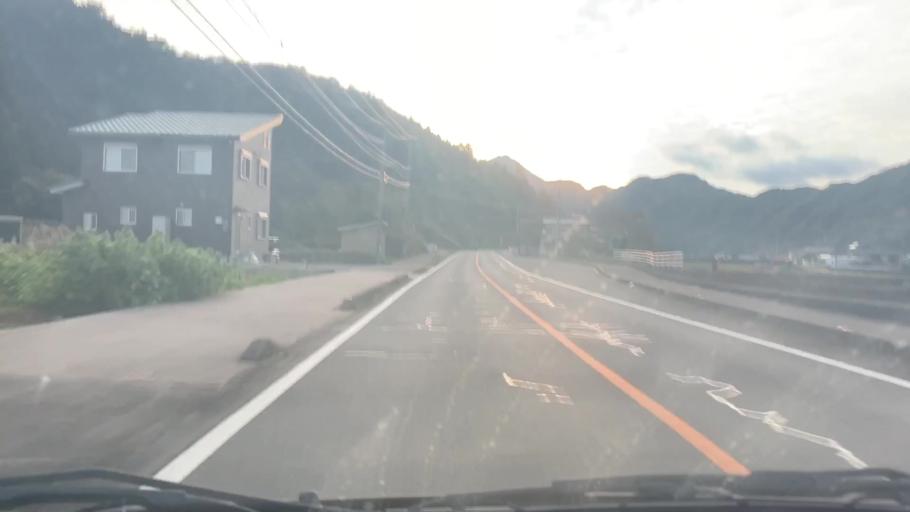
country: JP
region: Saga Prefecture
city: Kashima
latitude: 33.0872
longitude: 130.0799
